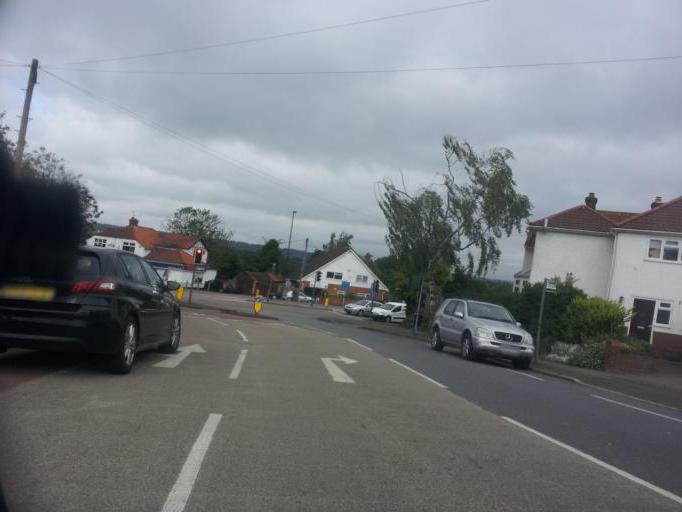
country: GB
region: England
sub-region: Kent
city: Maidstone
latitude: 51.2823
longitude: 0.5011
